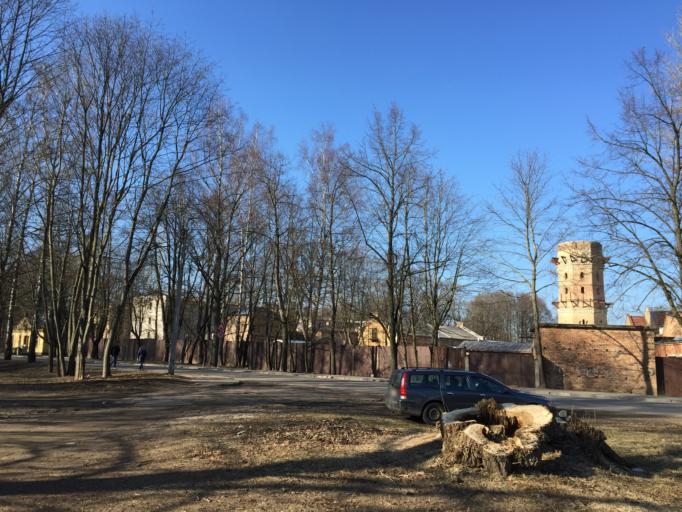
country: LV
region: Riga
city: Bergi
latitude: 56.9924
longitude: 24.2342
